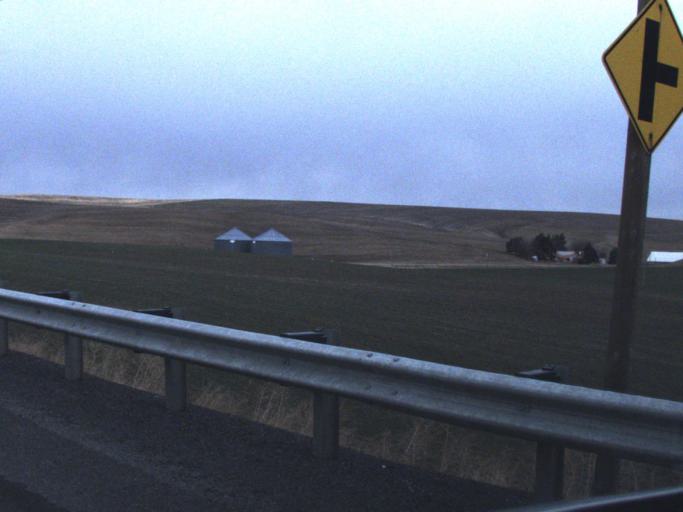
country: US
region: Washington
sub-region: Whitman County
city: Colfax
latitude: 46.8135
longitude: -117.6633
